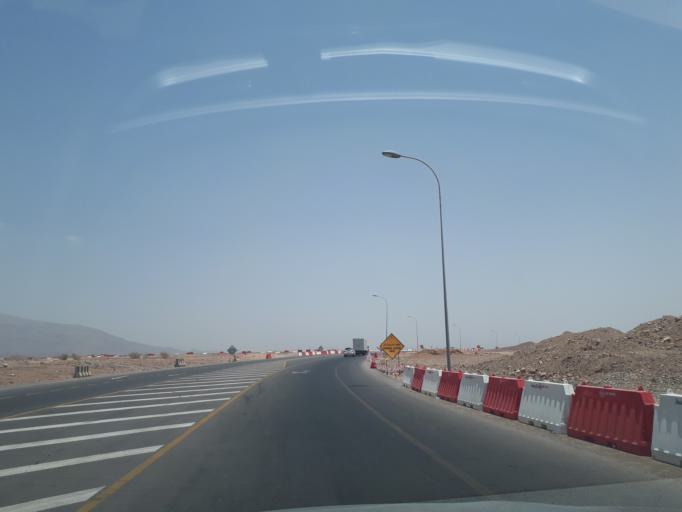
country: OM
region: Ash Sharqiyah
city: Badiyah
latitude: 22.4379
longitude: 59.0286
